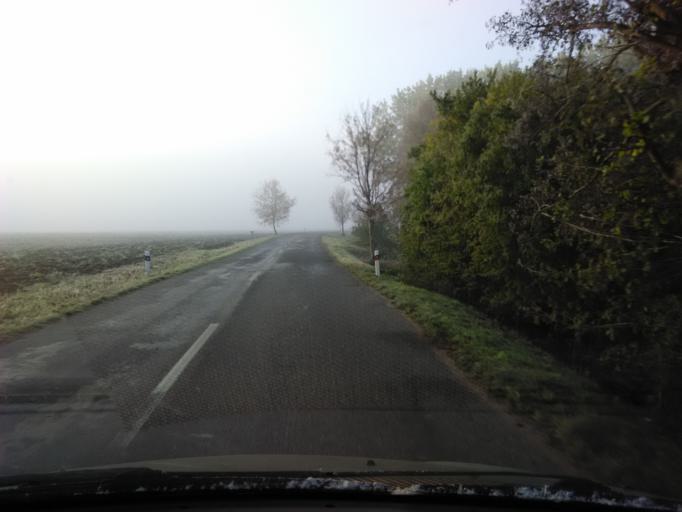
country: SK
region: Nitriansky
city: Tlmace
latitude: 48.2580
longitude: 18.5350
